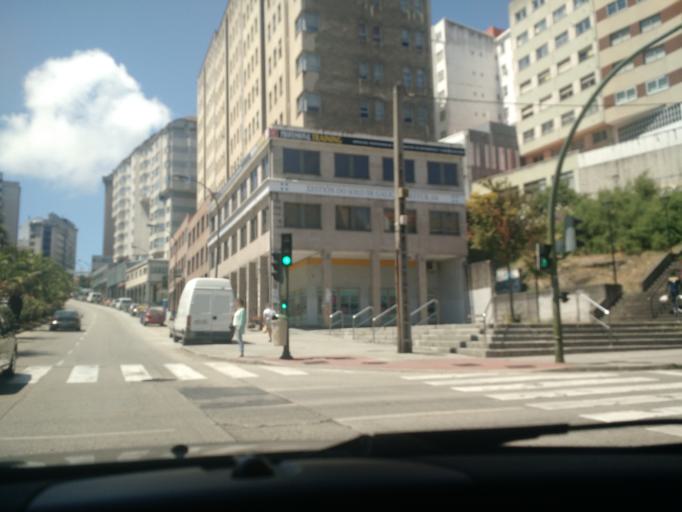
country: ES
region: Galicia
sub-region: Provincia da Coruna
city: A Coruna
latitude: 43.3581
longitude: -8.4056
